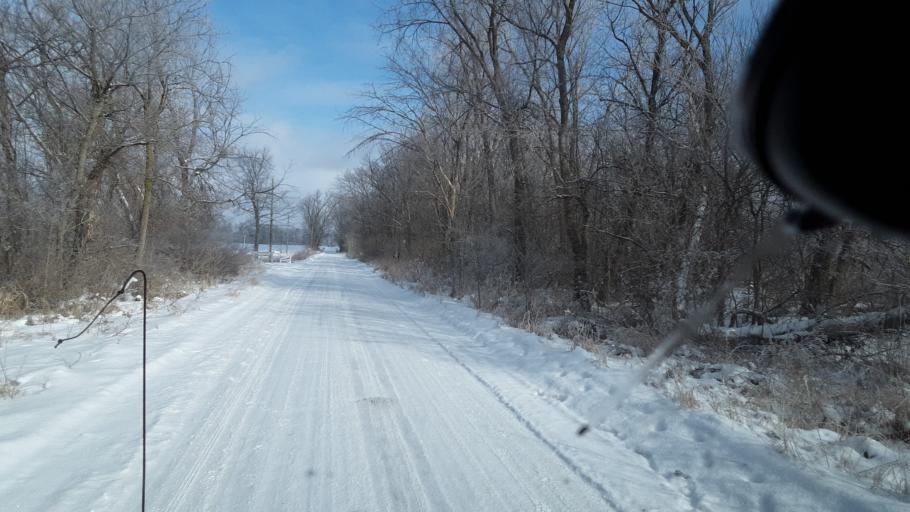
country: US
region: Michigan
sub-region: Eaton County
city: Eaton Rapids
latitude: 42.5122
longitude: -84.6309
